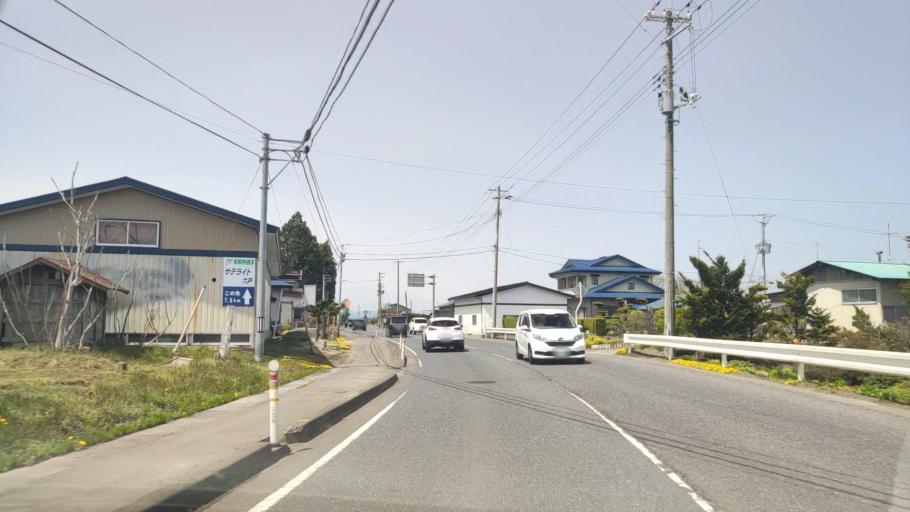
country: JP
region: Aomori
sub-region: Misawa Shi
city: Inuotose
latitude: 40.5913
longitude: 141.3487
